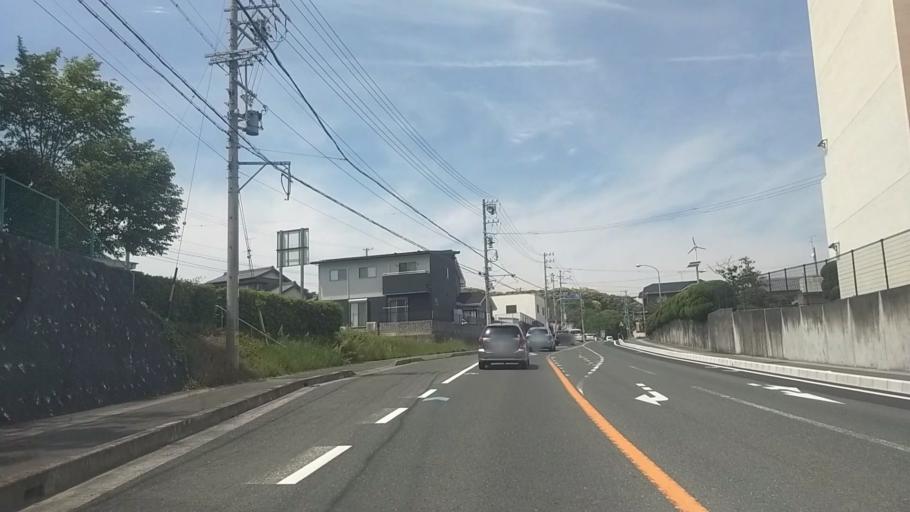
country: JP
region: Shizuoka
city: Kosai-shi
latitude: 34.7417
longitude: 137.5155
